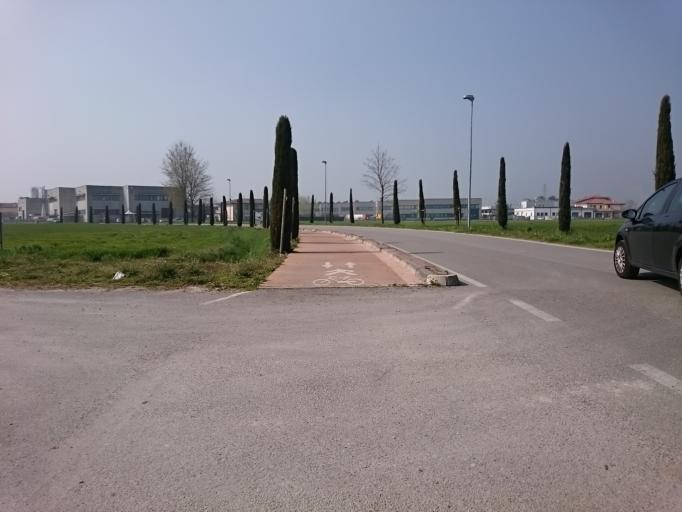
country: IT
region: Veneto
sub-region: Provincia di Padova
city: Pernumia
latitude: 45.2556
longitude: 11.7830
